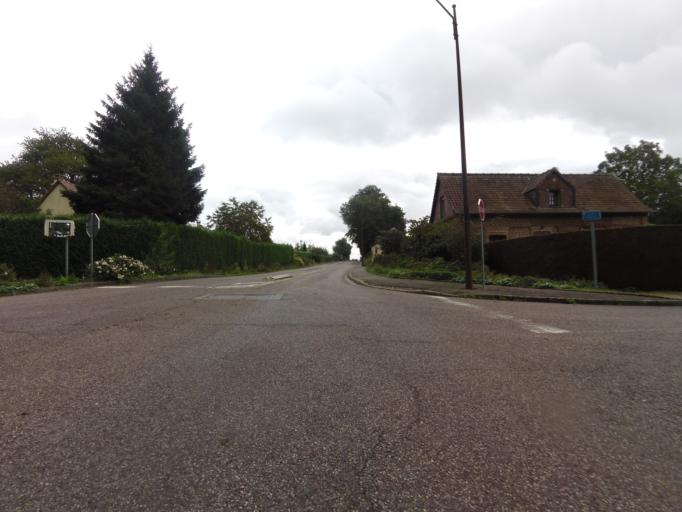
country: FR
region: Haute-Normandie
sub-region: Departement de la Seine-Maritime
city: Totes
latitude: 49.7189
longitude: 1.0550
